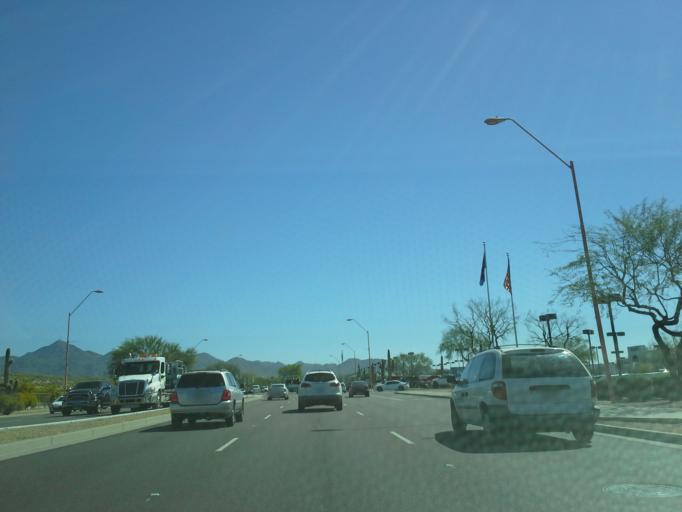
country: US
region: Arizona
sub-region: Maricopa County
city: Paradise Valley
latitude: 33.6357
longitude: -111.9140
